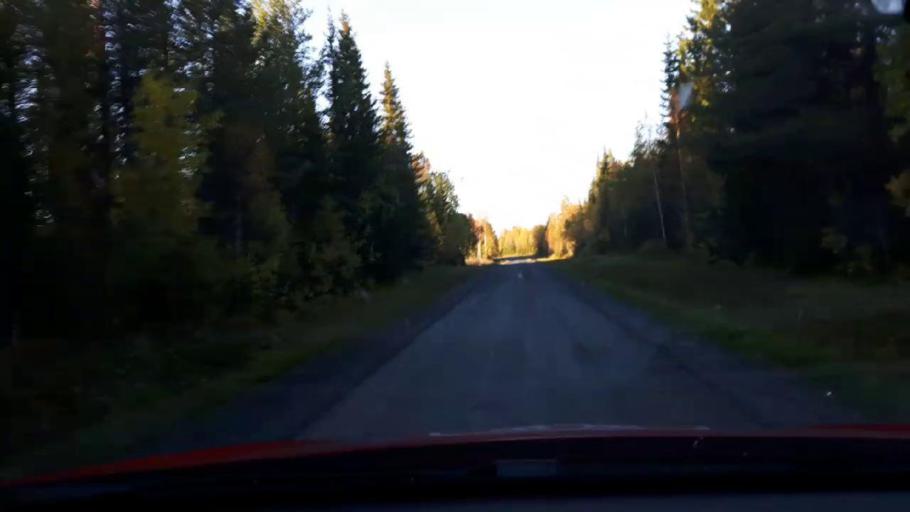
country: SE
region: Jaemtland
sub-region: Krokoms Kommun
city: Krokom
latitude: 63.4257
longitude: 14.6094
